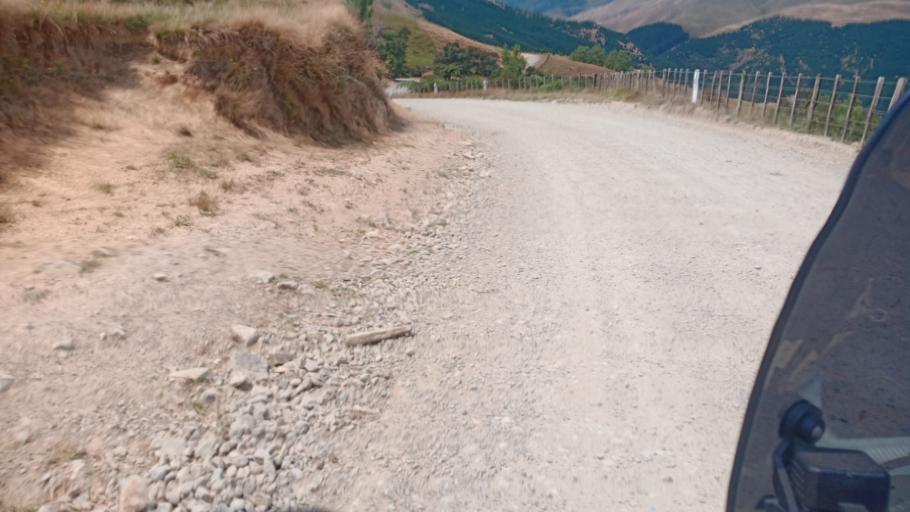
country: NZ
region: Bay of Plenty
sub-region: Opotiki District
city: Opotiki
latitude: -37.6569
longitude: 178.1284
